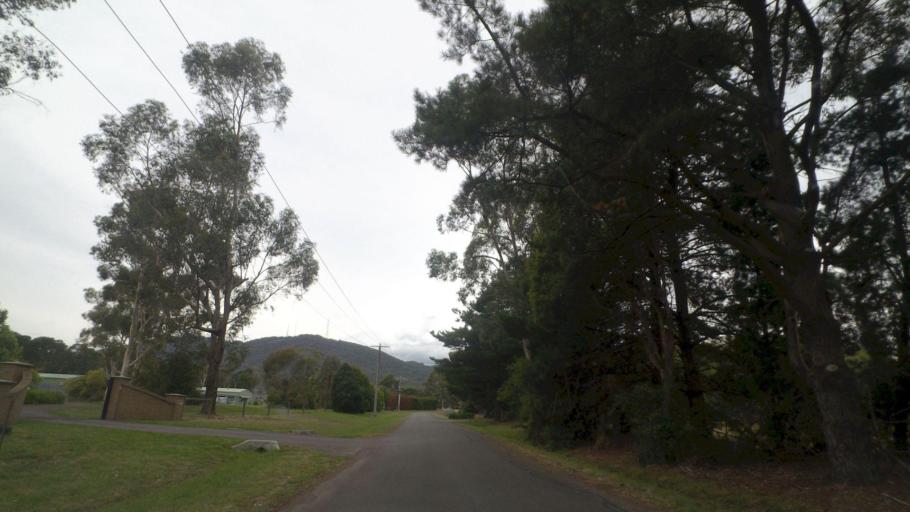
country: AU
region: Victoria
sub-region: Knox
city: The Basin
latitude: -37.8395
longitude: 145.3135
